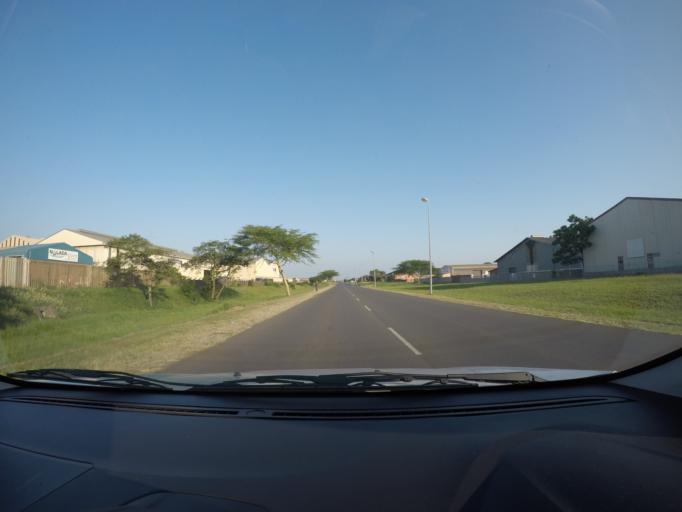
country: ZA
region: KwaZulu-Natal
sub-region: uThungulu District Municipality
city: Richards Bay
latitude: -28.7524
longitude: 32.0233
